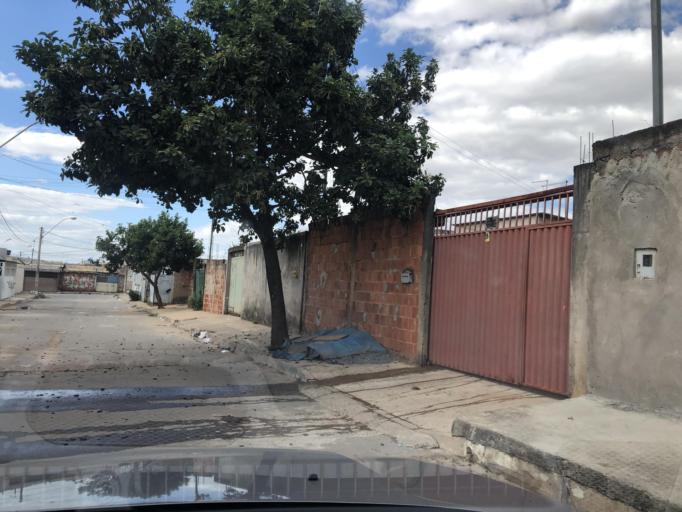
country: BR
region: Federal District
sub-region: Brasilia
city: Brasilia
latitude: -15.8870
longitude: -48.1457
